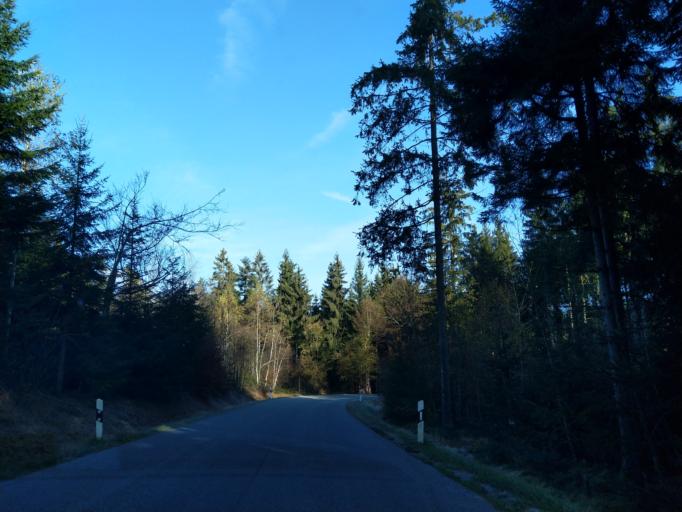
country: DE
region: Bavaria
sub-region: Lower Bavaria
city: Lalling
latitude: 48.8847
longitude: 13.1264
